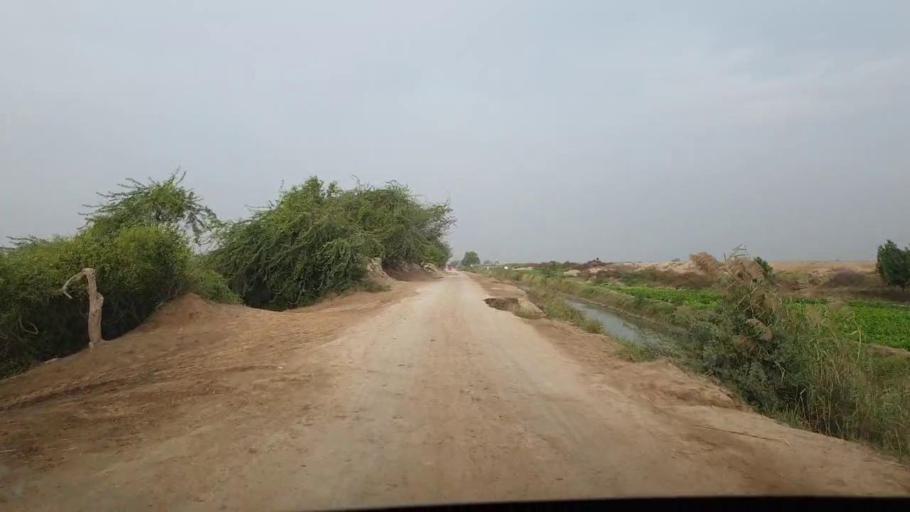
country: PK
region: Sindh
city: Chuhar Jamali
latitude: 24.3980
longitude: 67.9703
